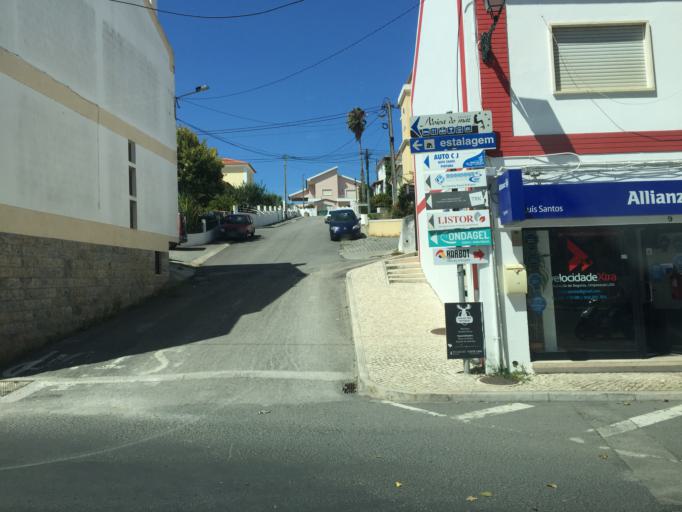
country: PT
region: Lisbon
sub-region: Lourinha
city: Lourinha
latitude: 39.2386
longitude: -9.3128
